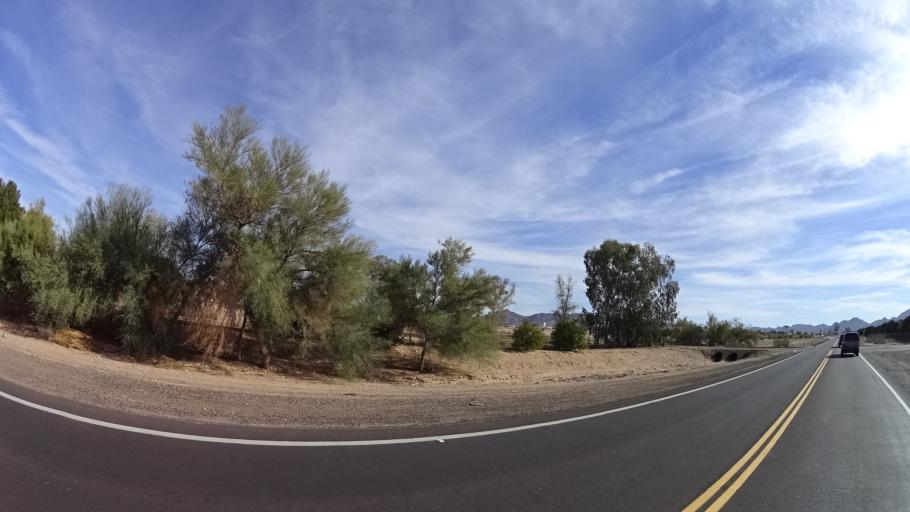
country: US
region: Arizona
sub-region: Maricopa County
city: Queen Creek
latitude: 33.2277
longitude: -111.6859
